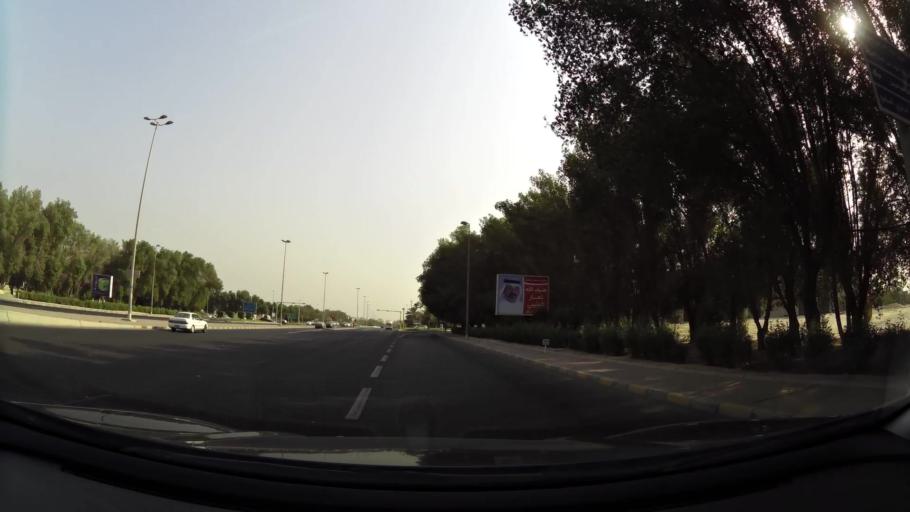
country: KW
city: Al Funaytis
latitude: 29.2104
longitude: 48.0902
